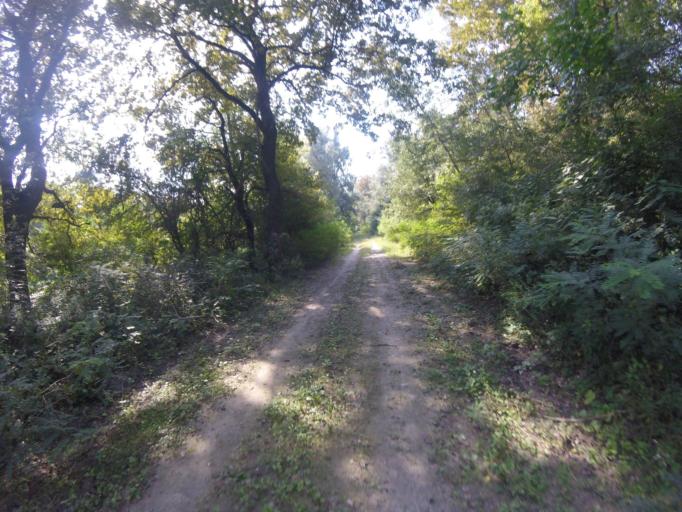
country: HU
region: Bacs-Kiskun
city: Baja
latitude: 46.2153
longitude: 18.8886
